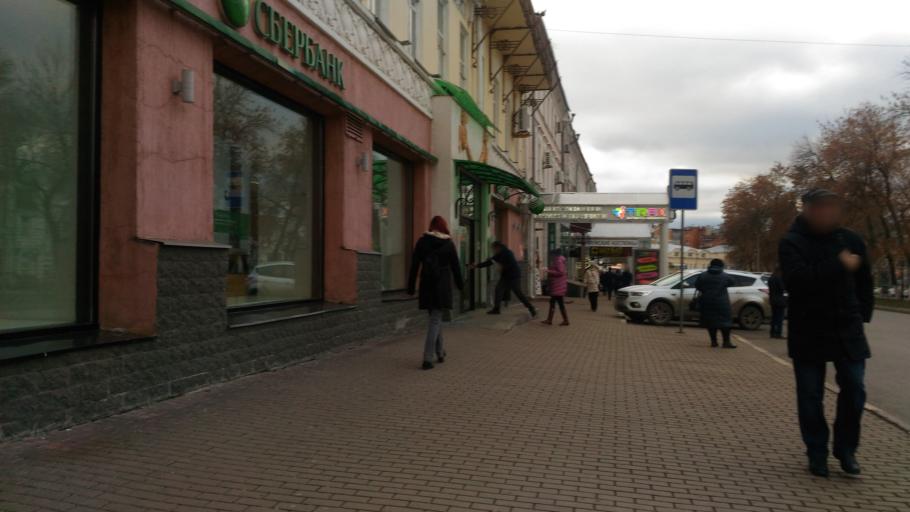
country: RU
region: Ulyanovsk
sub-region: Ulyanovskiy Rayon
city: Ulyanovsk
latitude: 54.3177
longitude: 48.3965
